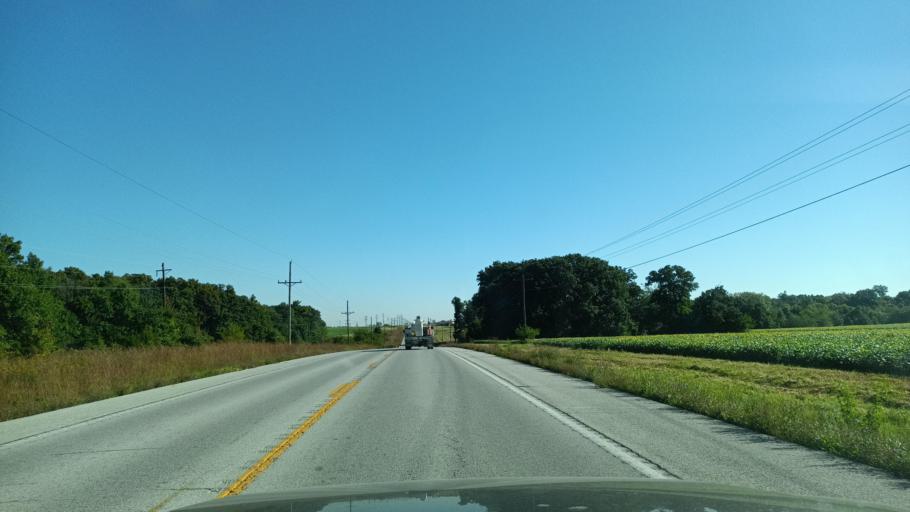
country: US
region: Missouri
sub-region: Audrain County
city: Vandalia
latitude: 39.4603
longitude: -91.6113
